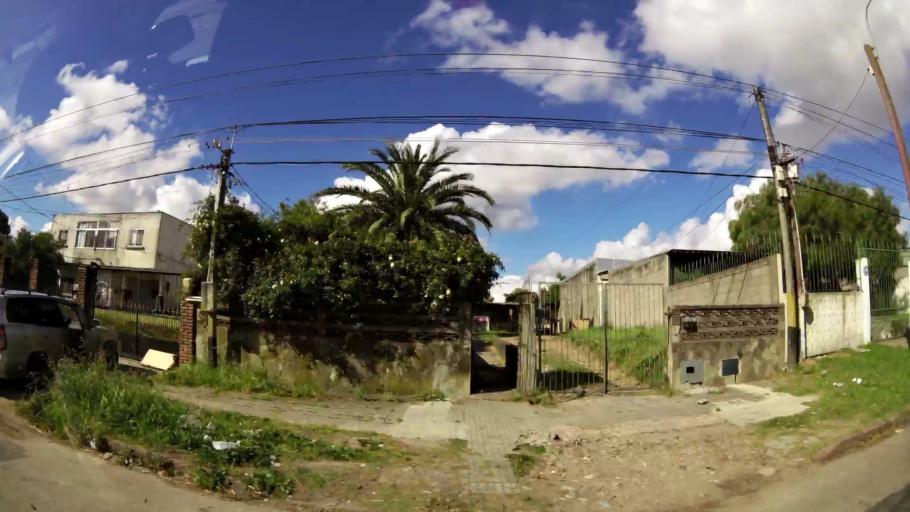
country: UY
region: Canelones
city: La Paz
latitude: -34.8116
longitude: -56.2270
